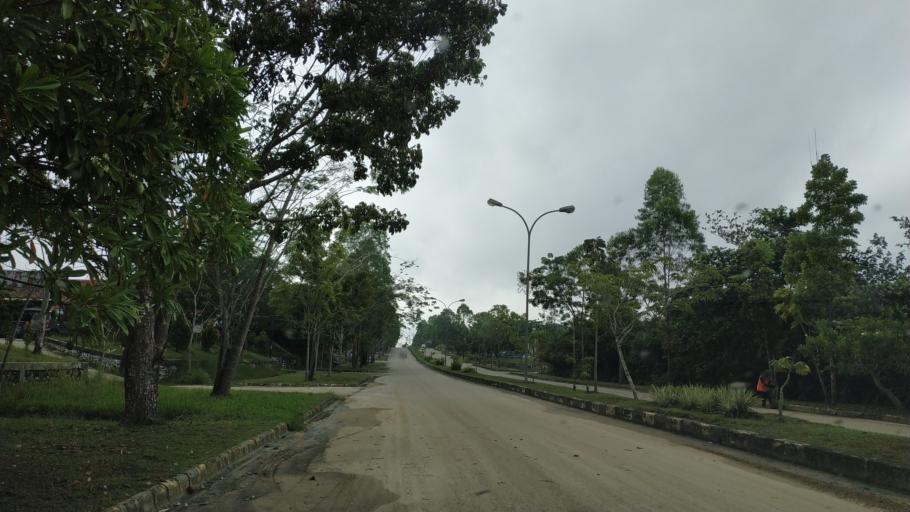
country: ID
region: Riau
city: Pangkalanbunut
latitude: 0.3822
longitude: 101.8241
